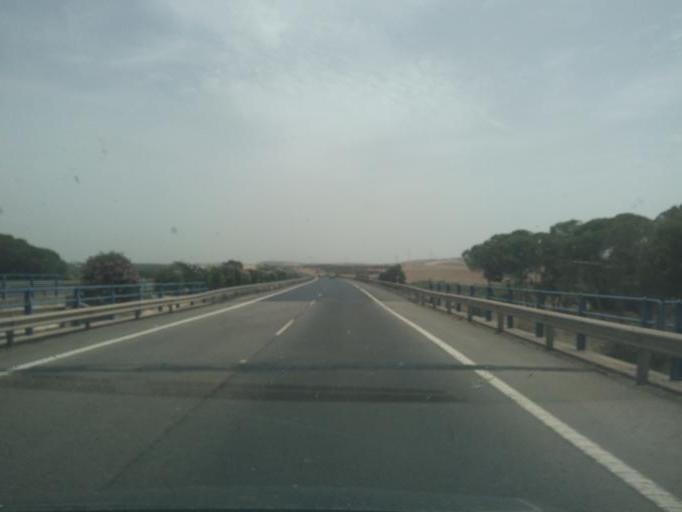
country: ES
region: Andalusia
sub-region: Provincia de Huelva
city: Bonares
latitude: 37.3401
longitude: -6.7112
